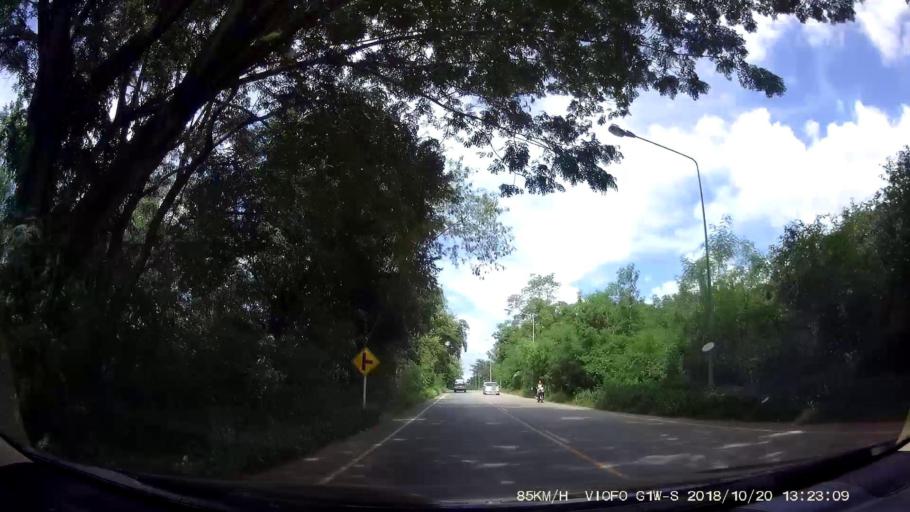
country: TH
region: Chaiyaphum
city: Khon San
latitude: 16.5804
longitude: 101.9200
